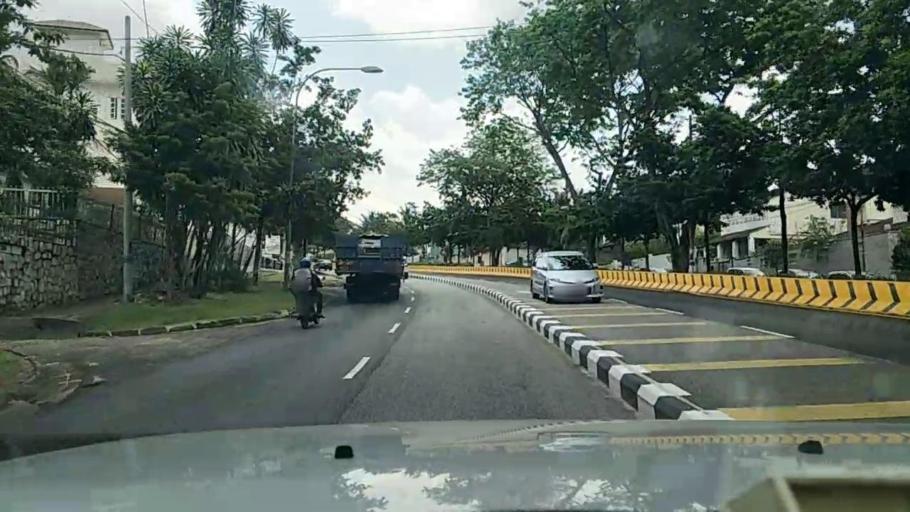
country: MY
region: Kuala Lumpur
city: Kuala Lumpur
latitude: 3.1416
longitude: 101.6715
